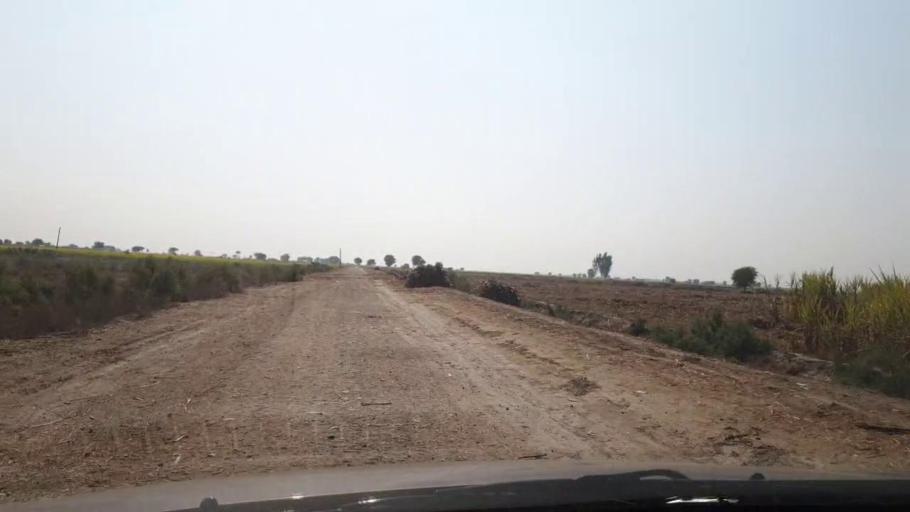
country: PK
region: Sindh
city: Jhol
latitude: 25.8647
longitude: 68.9981
